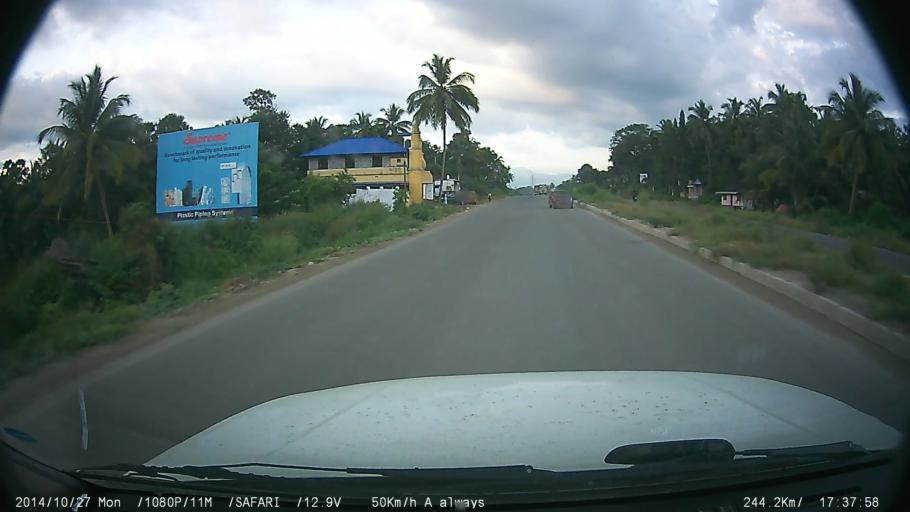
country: IN
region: Kerala
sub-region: Palakkad district
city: Palakkad
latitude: 10.6997
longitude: 76.5912
